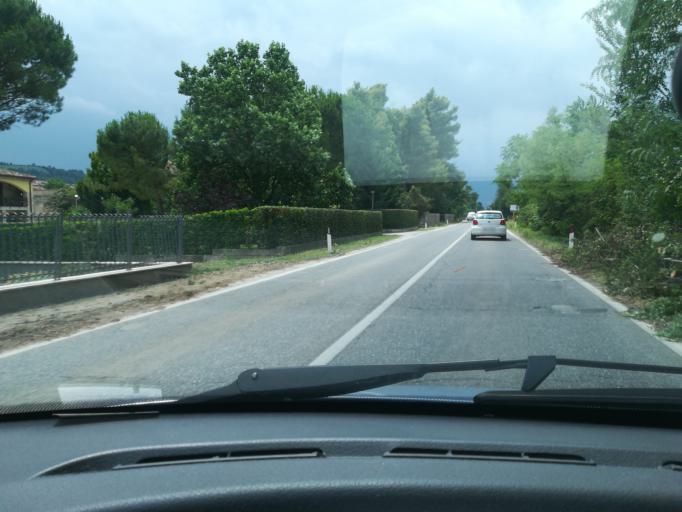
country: IT
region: The Marches
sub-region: Provincia di Macerata
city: Montecassiano
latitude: 43.3491
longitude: 13.4634
